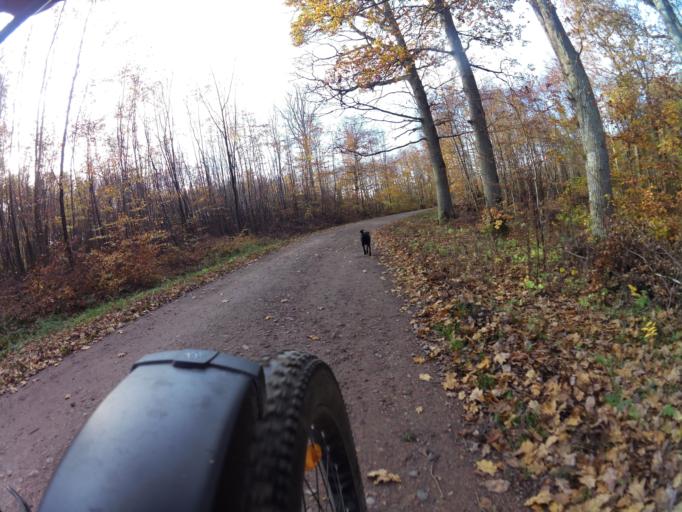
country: PL
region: Pomeranian Voivodeship
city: Strzelno
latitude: 54.7394
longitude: 18.2712
